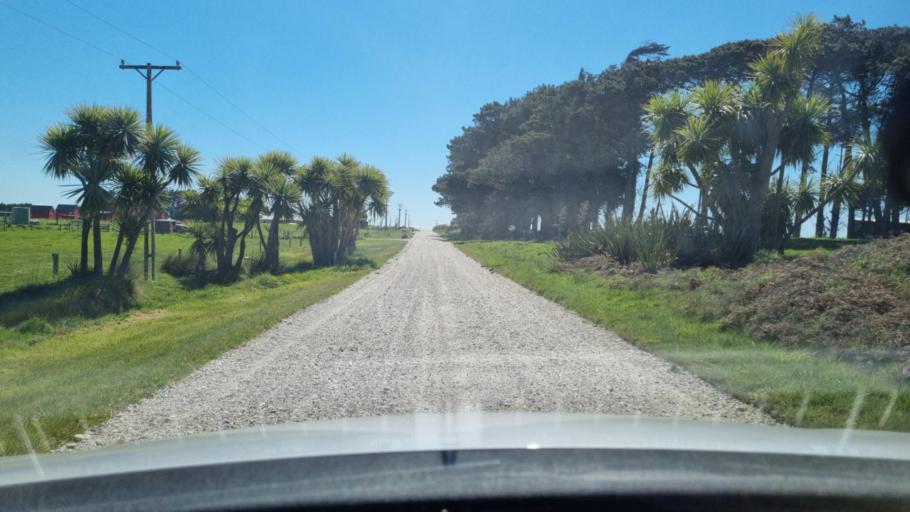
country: NZ
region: Southland
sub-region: Invercargill City
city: Invercargill
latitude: -46.4142
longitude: 168.2633
